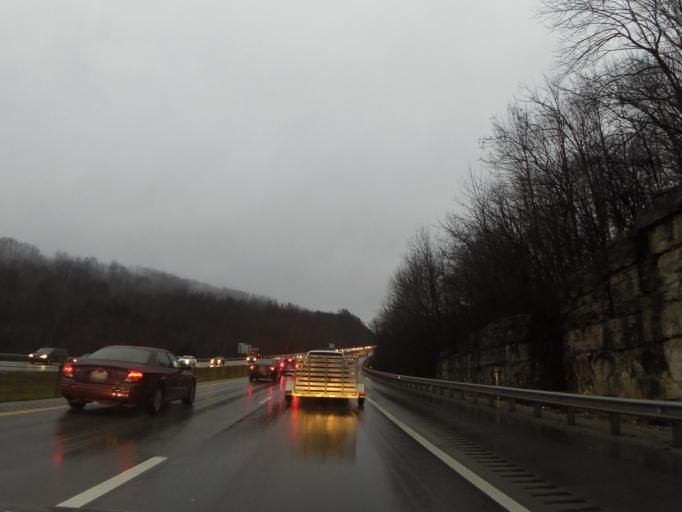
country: US
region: Kentucky
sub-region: Rockcastle County
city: Mount Vernon
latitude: 37.3370
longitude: -84.3060
